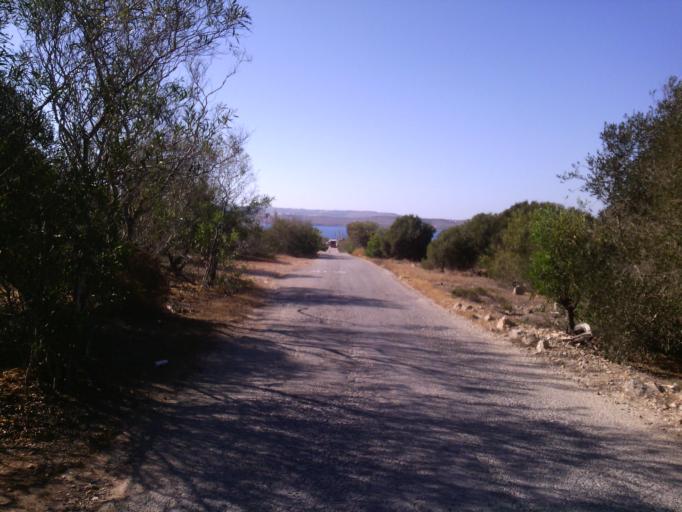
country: MT
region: Il-Mellieha
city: Mellieha
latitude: 35.9801
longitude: 14.3533
